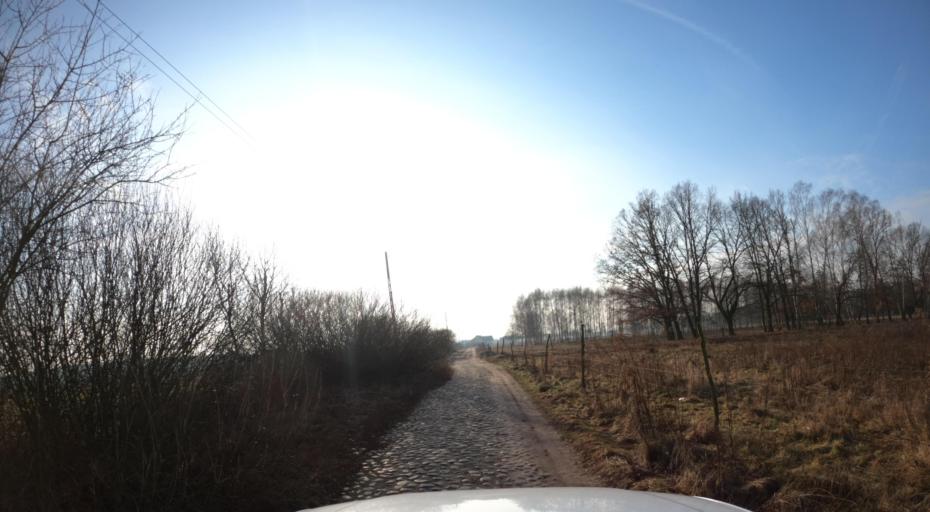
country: PL
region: Lubusz
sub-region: Powiat gorzowski
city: Kostrzyn nad Odra
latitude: 52.6209
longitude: 14.6254
